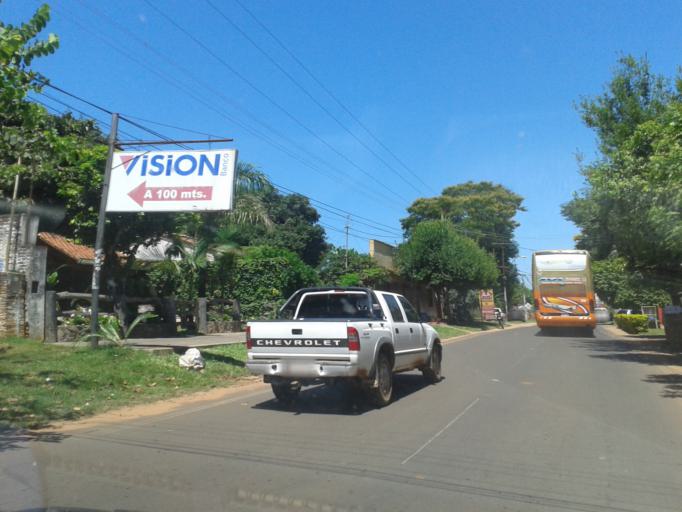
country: PY
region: Misiones
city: Santa Maria
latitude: -26.8863
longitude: -57.0213
